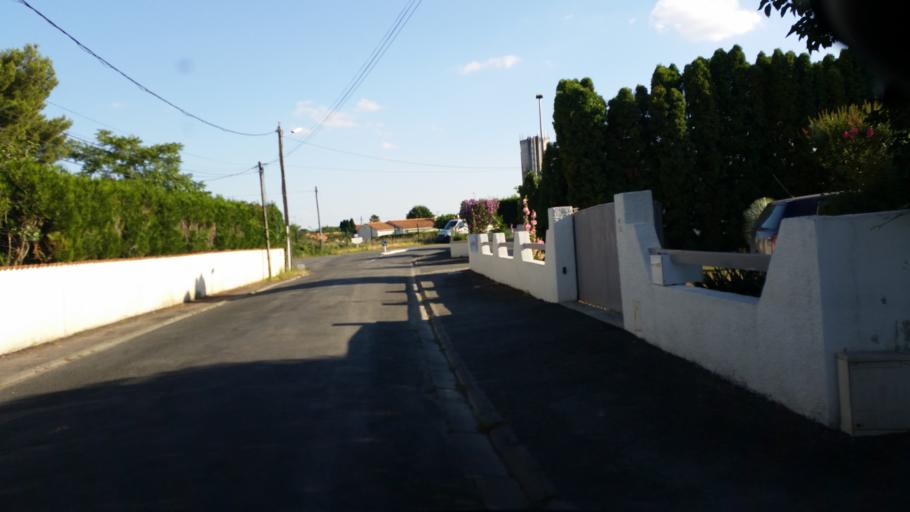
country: FR
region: Poitou-Charentes
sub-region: Departement de la Charente-Maritime
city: Marans
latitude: 46.3048
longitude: -0.9833
